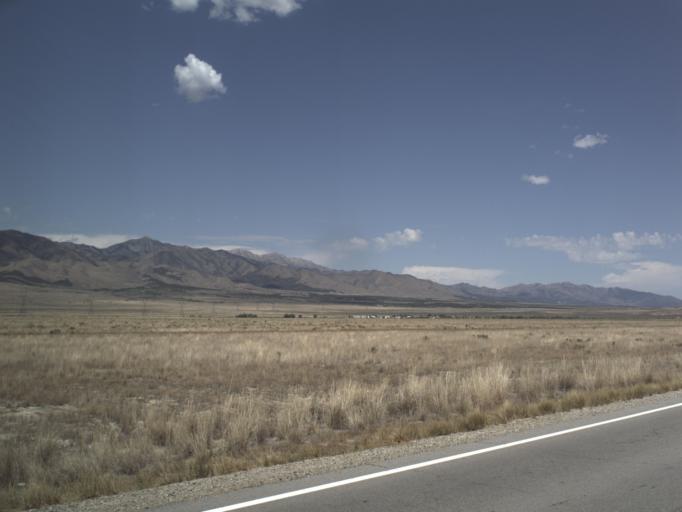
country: US
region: Utah
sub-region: Tooele County
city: Tooele
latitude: 40.3579
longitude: -112.4135
